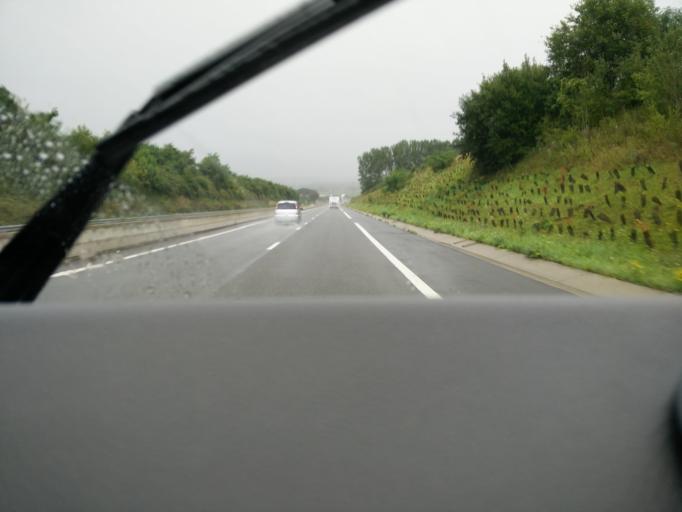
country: FR
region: Nord-Pas-de-Calais
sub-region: Departement du Pas-de-Calais
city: Marconnelle
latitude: 50.3626
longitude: 2.0127
